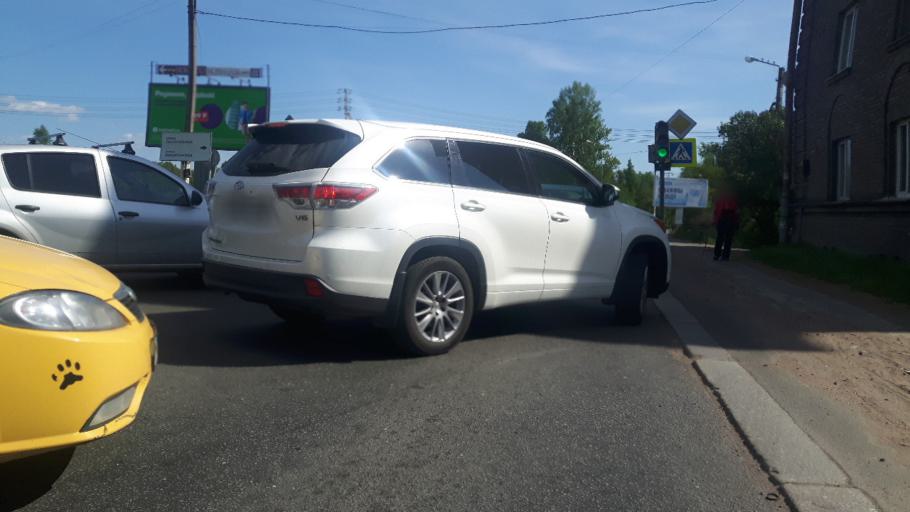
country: RU
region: Leningrad
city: Vyborg
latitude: 60.7208
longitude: 28.7180
